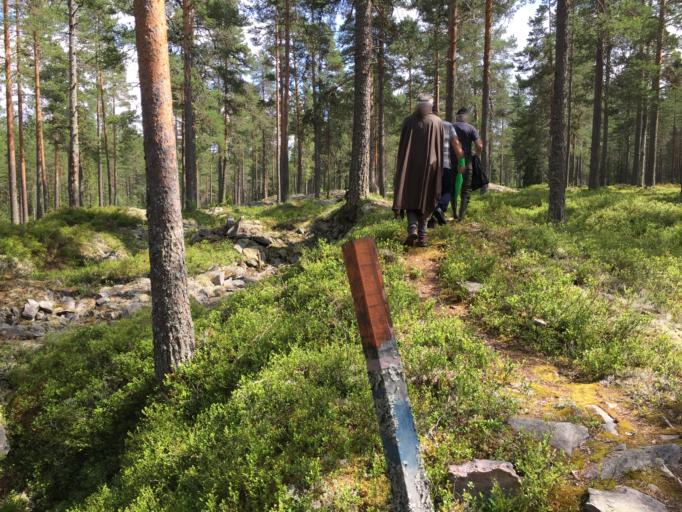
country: SE
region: Dalarna
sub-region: Malung-Saelens kommun
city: Malung
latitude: 60.6465
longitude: 13.7654
